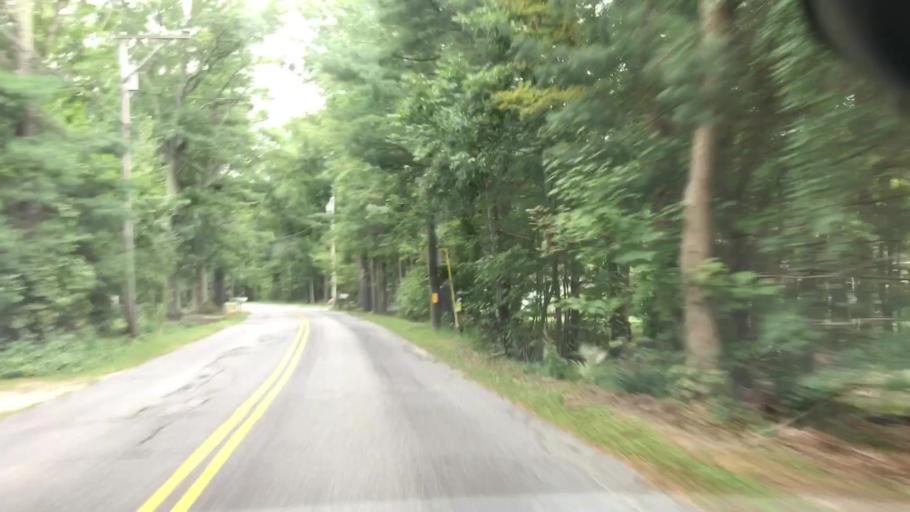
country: US
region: New Hampshire
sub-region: Hillsborough County
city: Merrimack
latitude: 42.8221
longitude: -71.5627
